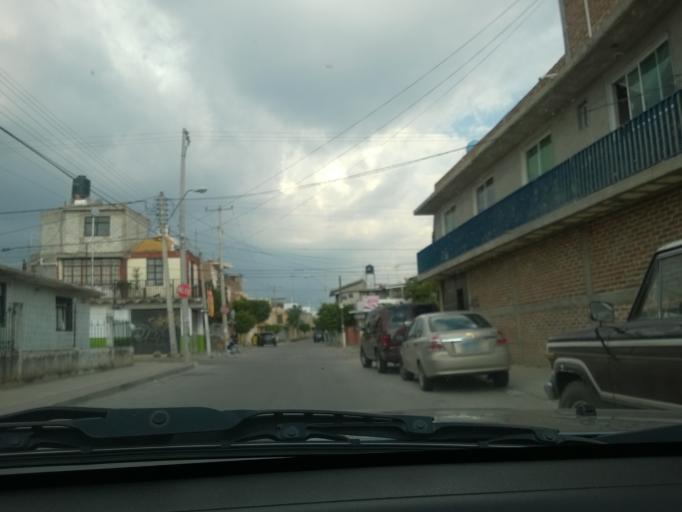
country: MX
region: Guanajuato
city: Leon
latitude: 21.1276
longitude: -101.6507
